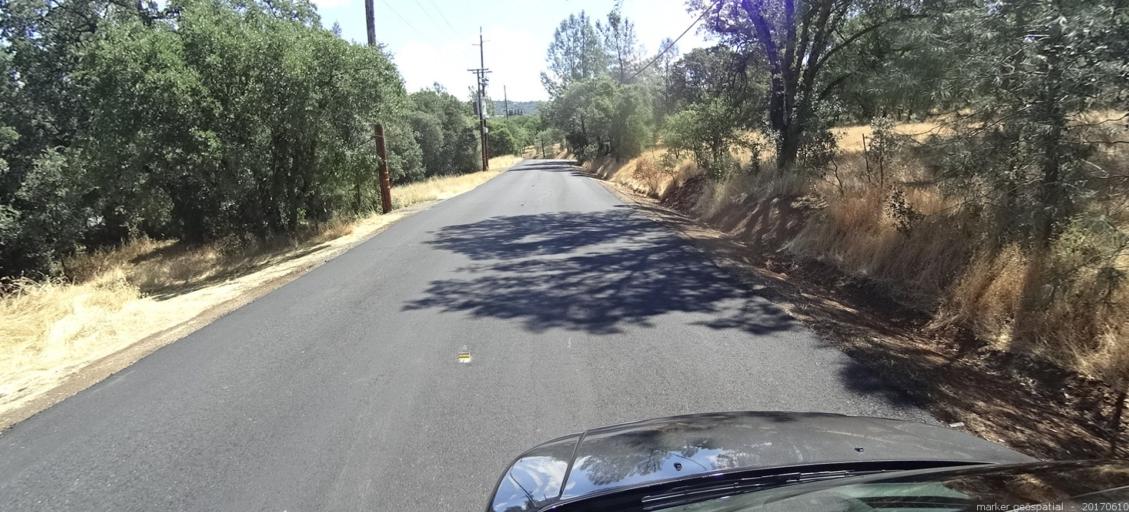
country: US
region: California
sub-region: Butte County
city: Oroville East
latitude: 39.5073
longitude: -121.5063
